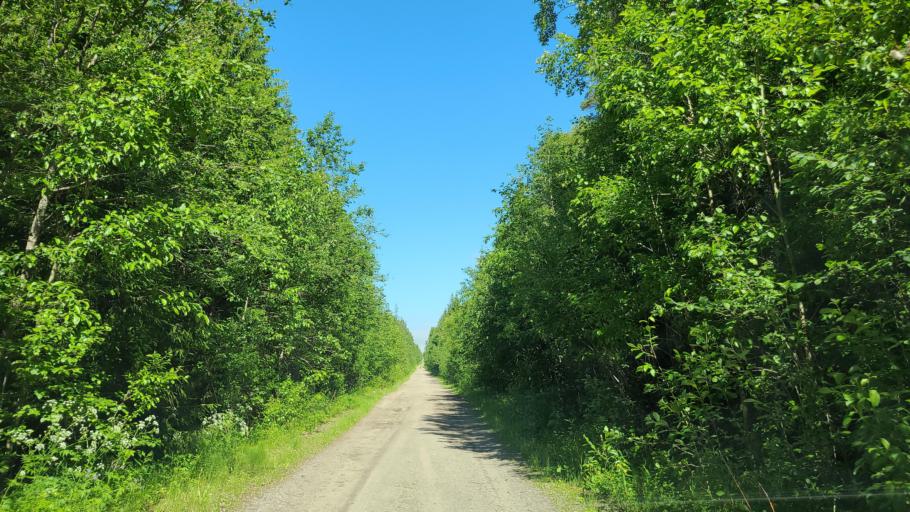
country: SE
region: Vaesternorrland
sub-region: OErnskoeldsviks Kommun
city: Husum
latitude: 63.4215
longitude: 19.2237
